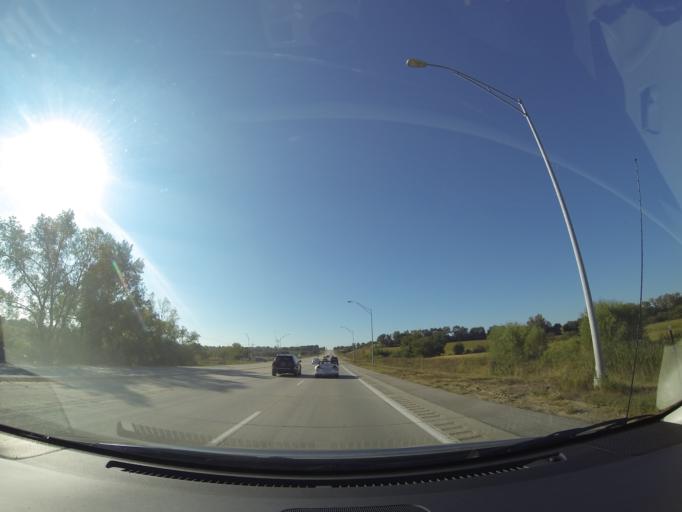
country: US
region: Nebraska
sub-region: Sarpy County
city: Gretna
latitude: 41.1771
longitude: -96.2343
